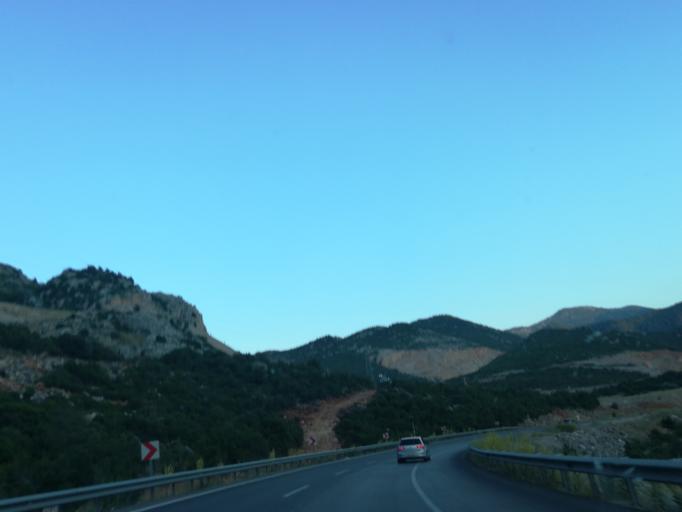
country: TR
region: Antalya
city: Dagbeli
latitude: 37.1603
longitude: 30.5104
